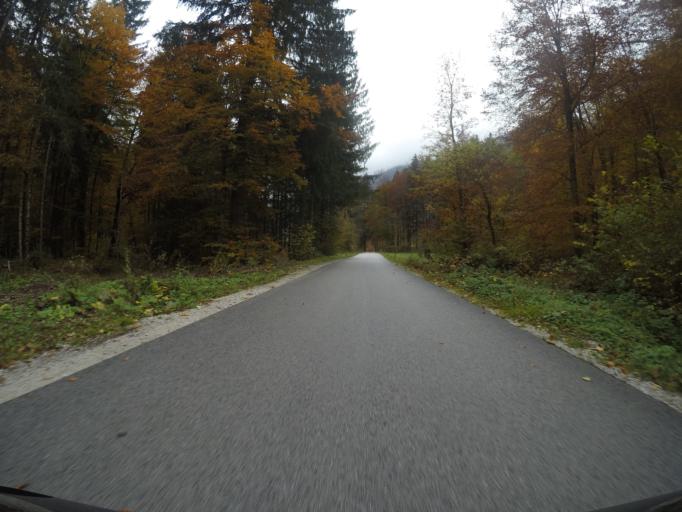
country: SI
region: Jesenice
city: Hrusica
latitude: 46.4258
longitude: 13.9720
